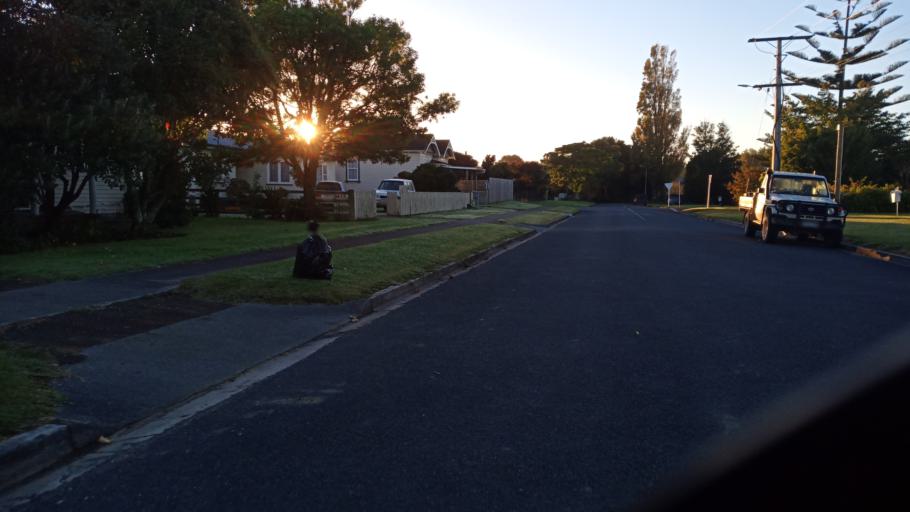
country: NZ
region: Gisborne
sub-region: Gisborne District
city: Gisborne
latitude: -38.6623
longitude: 177.9908
